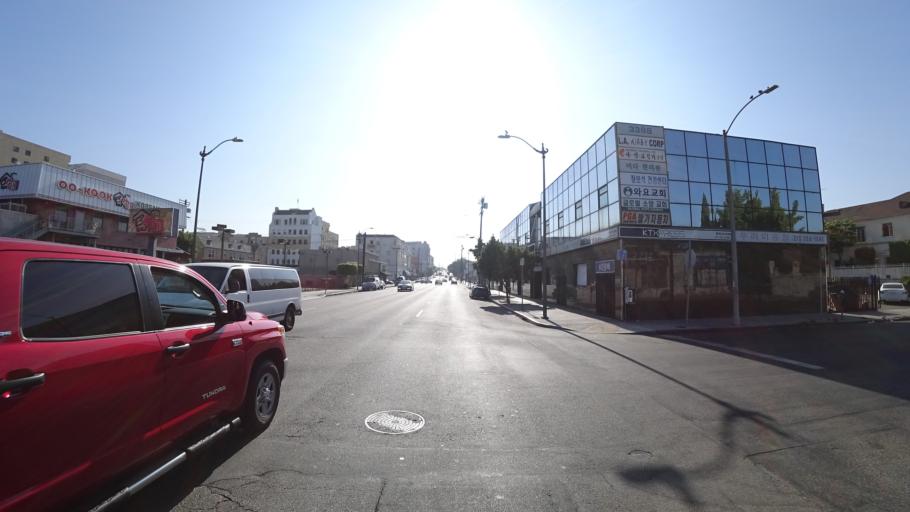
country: US
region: California
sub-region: Los Angeles County
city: Silver Lake
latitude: 34.0576
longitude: -118.3033
